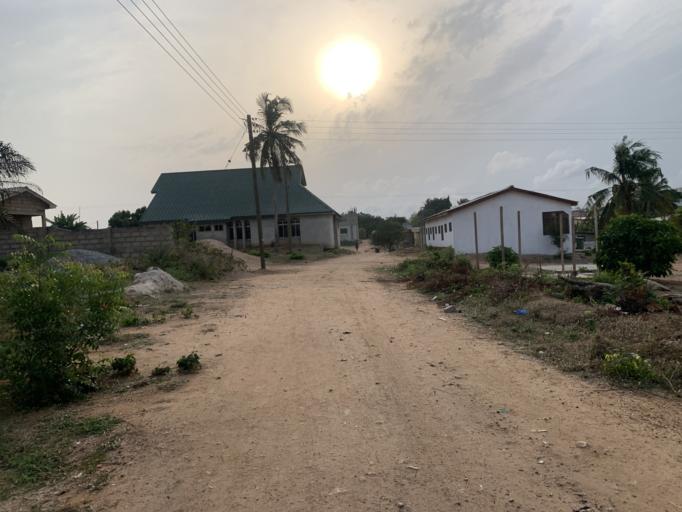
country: GH
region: Central
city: Winneba
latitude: 5.3606
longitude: -0.6262
